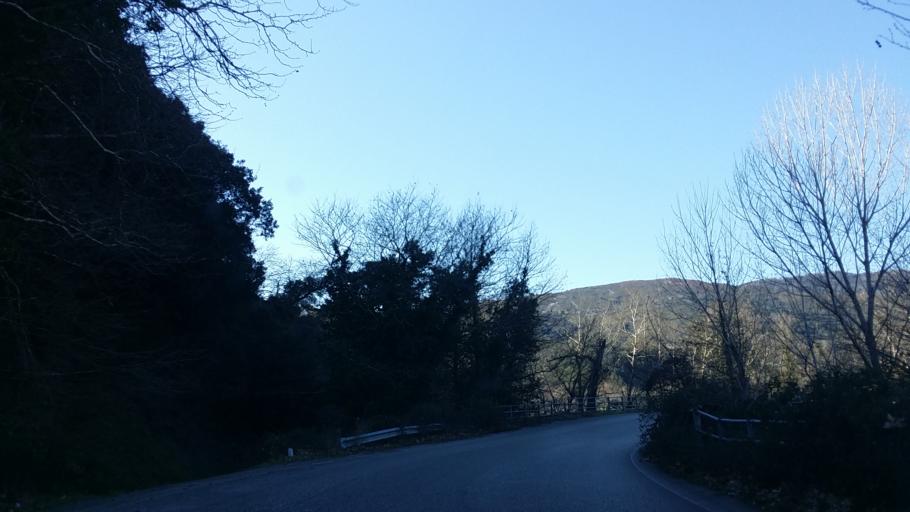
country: GR
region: West Greece
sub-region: Nomos Aitolias kai Akarnanias
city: Sardinia
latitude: 38.8536
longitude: 21.3381
